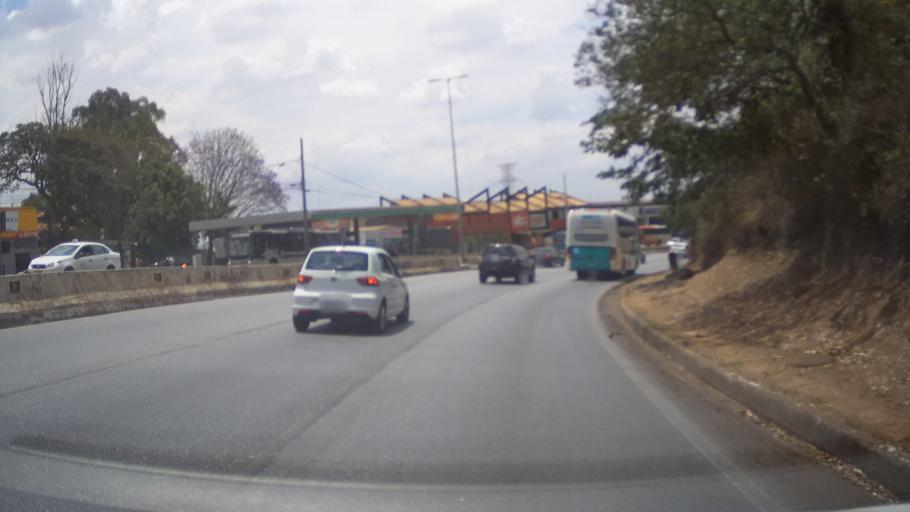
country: BR
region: Minas Gerais
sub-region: Belo Horizonte
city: Belo Horizonte
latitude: -19.9615
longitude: -43.9447
